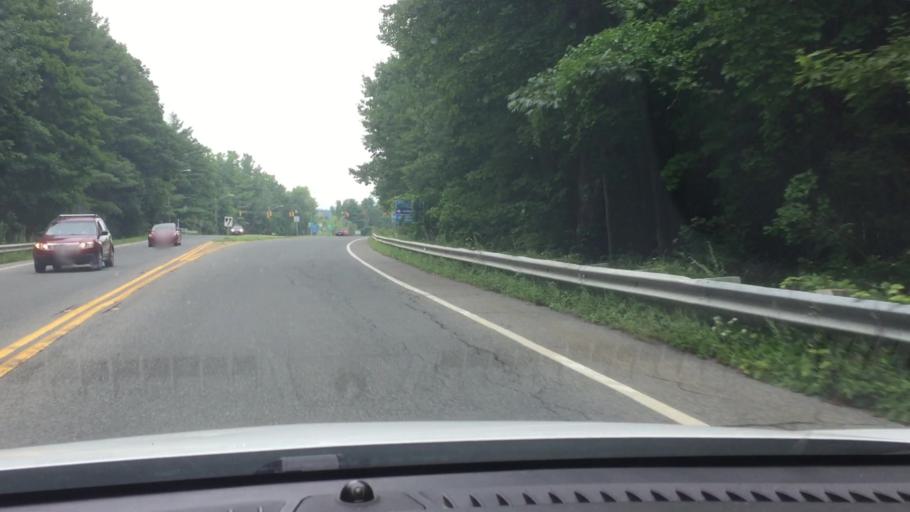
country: US
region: Massachusetts
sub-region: Berkshire County
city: Lenox
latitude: 42.3342
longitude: -73.2851
